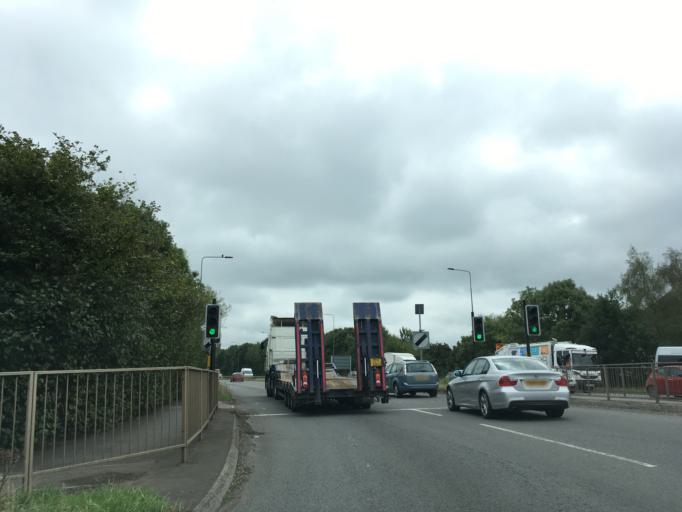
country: GB
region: England
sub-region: South Gloucestershire
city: Mangotsfield
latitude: 51.4989
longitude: -2.4796
